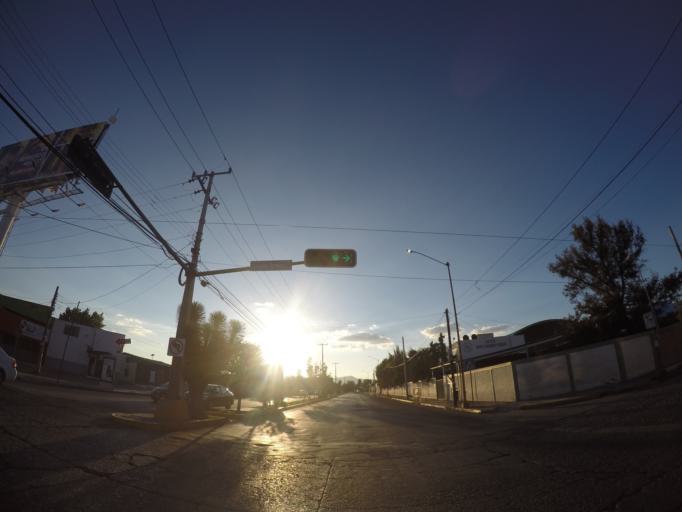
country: MX
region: San Luis Potosi
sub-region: San Luis Potosi
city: San Luis Potosi
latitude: 22.1373
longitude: -100.9850
